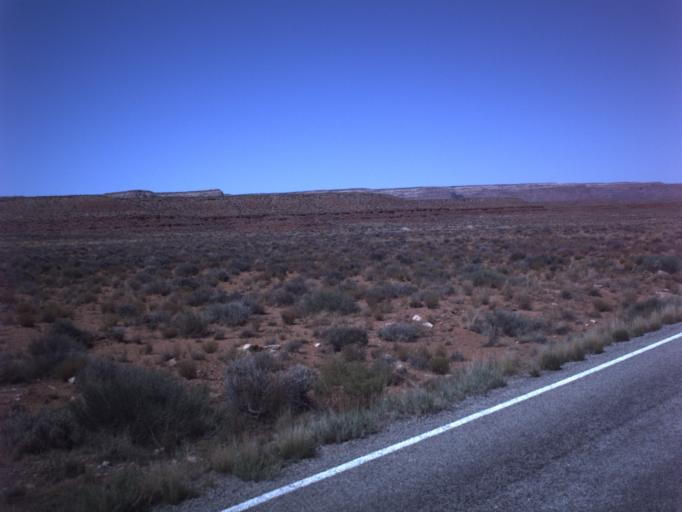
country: US
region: Arizona
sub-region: Navajo County
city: Kayenta
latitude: 37.1797
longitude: -109.9234
